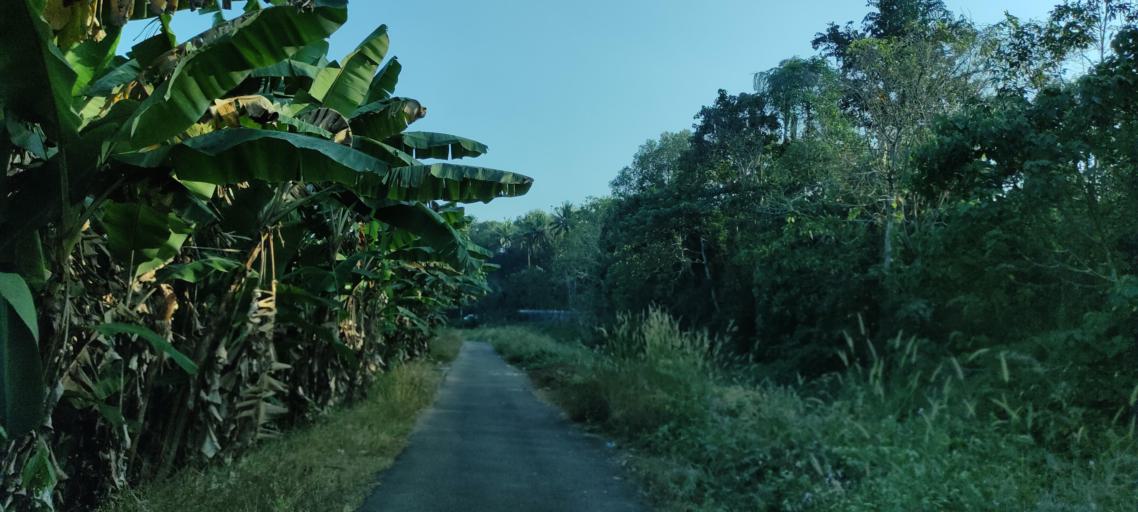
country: IN
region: Kerala
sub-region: Pattanamtitta
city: Adur
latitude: 9.1378
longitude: 76.7323
